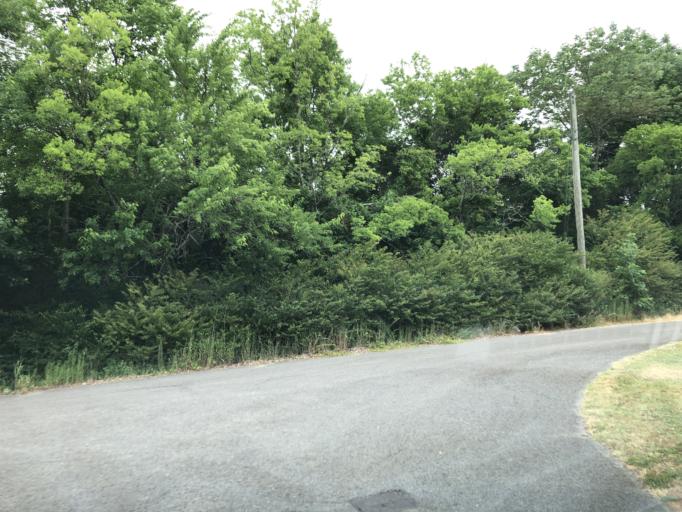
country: US
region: Tennessee
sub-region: Davidson County
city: Goodlettsville
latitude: 36.2917
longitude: -86.7269
